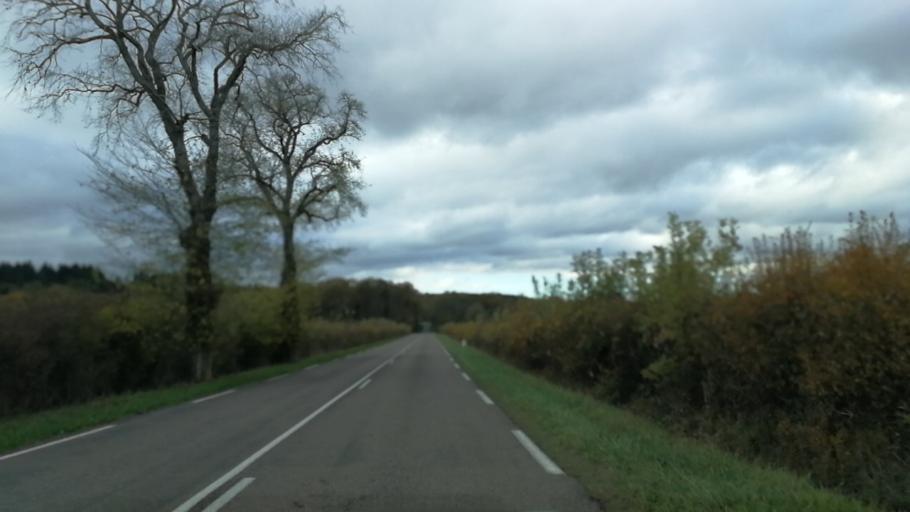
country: FR
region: Bourgogne
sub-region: Departement de la Cote-d'Or
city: Saulieu
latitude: 47.2575
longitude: 4.3279
